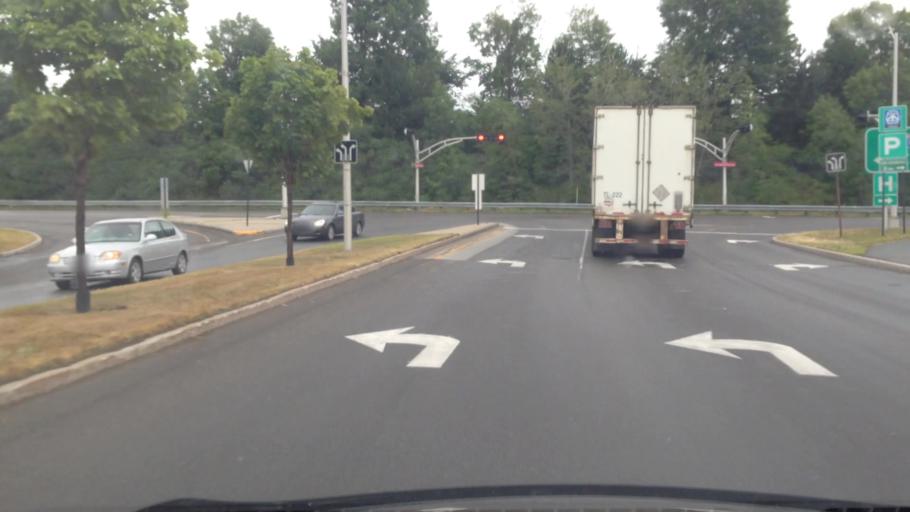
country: CA
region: Quebec
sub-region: Laurentides
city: Saint-Jerome
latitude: 45.7615
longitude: -74.0161
